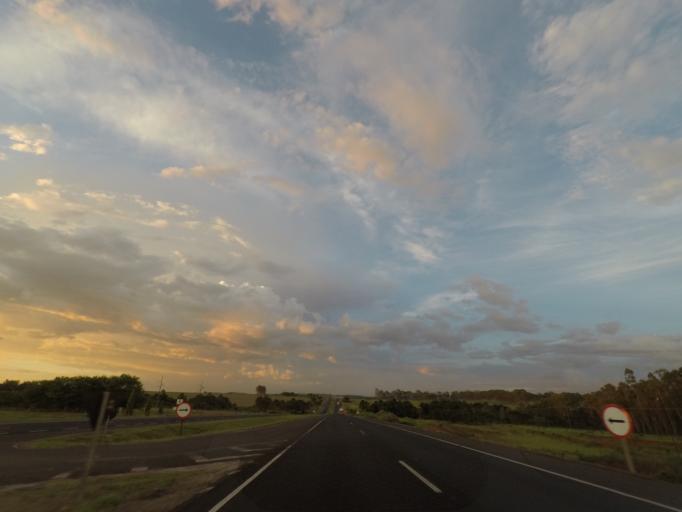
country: BR
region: Minas Gerais
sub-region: Uberaba
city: Uberaba
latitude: -19.6375
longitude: -48.0109
